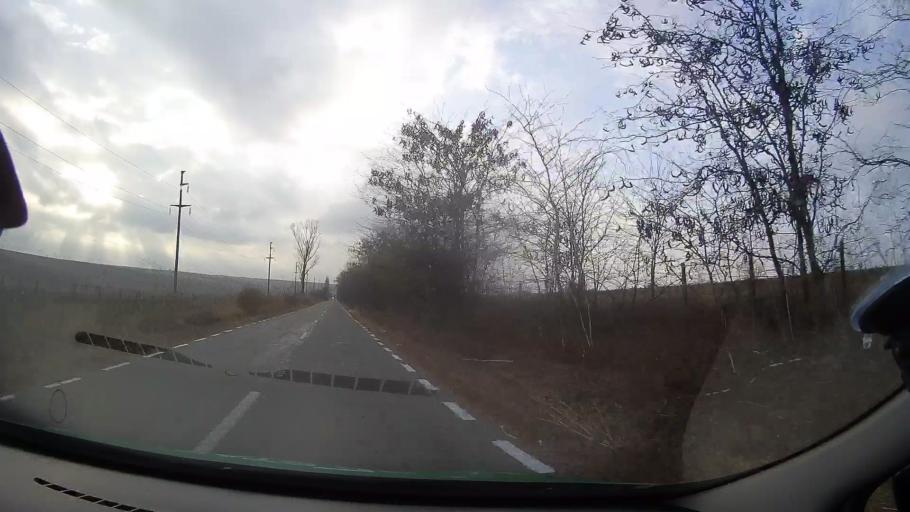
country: RO
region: Constanta
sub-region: Comuna Mircea Voda
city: Satu Nou
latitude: 44.2372
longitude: 28.2433
